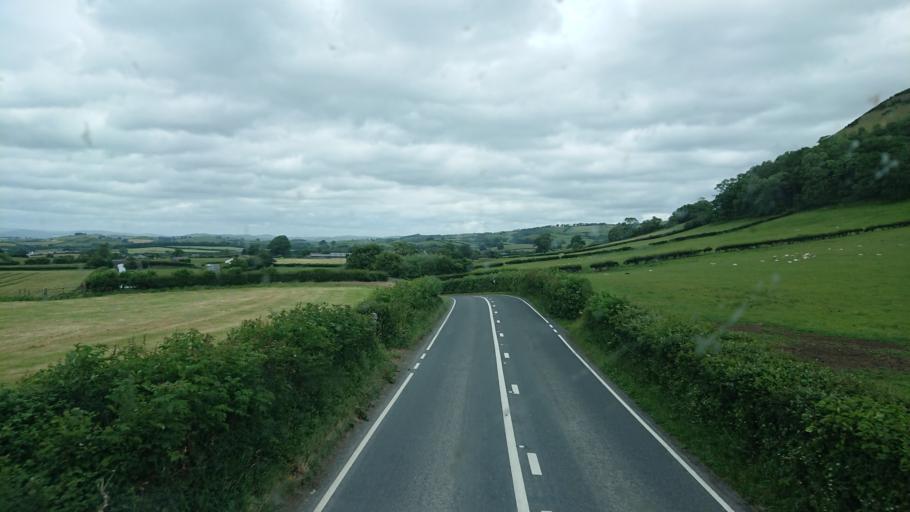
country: GB
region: England
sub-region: Cumbria
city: Milnthorpe
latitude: 54.2171
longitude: -2.7186
